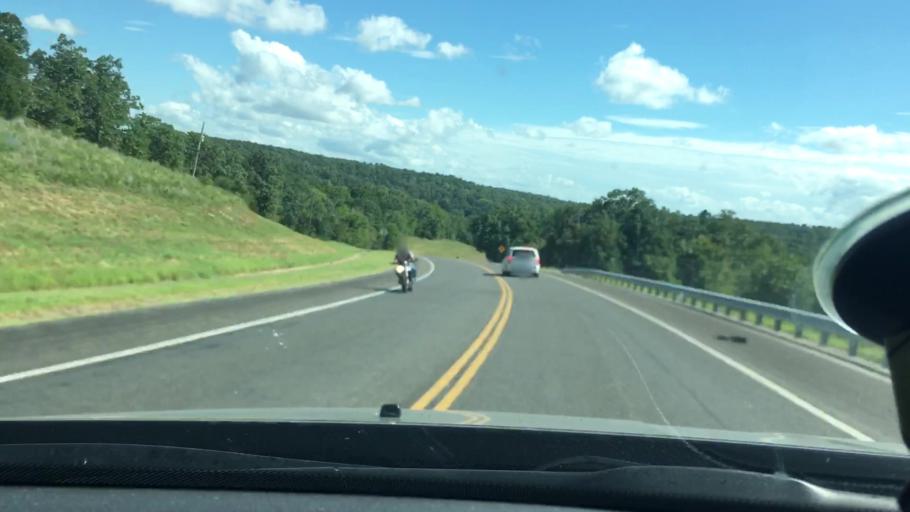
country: US
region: Oklahoma
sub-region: Sequoyah County
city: Vian
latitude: 35.5455
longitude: -94.9697
